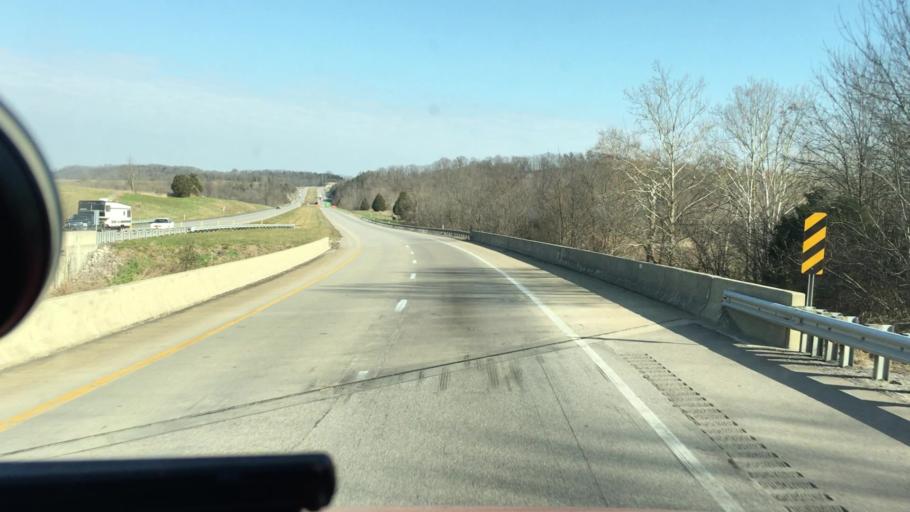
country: US
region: Kentucky
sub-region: Bath County
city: Owingsville
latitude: 38.1123
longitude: -83.8060
